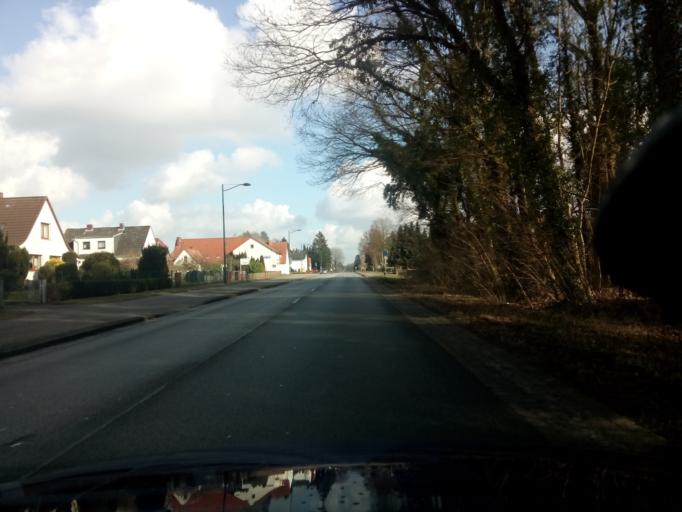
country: DE
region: Lower Saxony
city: Hambergen
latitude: 53.3159
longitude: 8.8654
